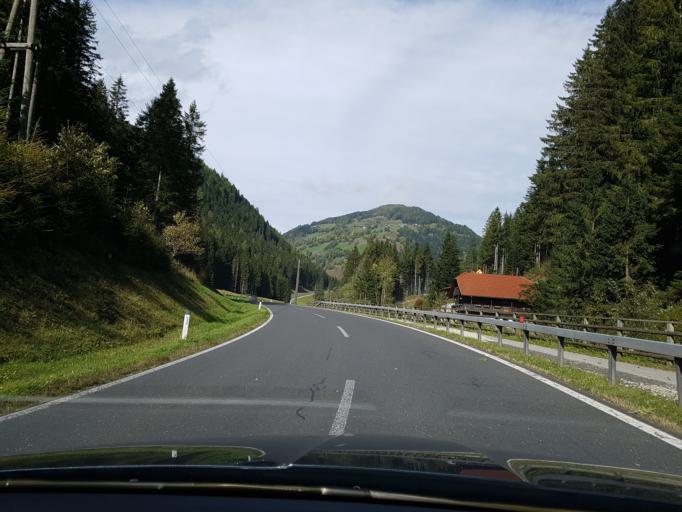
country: AT
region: Carinthia
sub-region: Politischer Bezirk Spittal an der Drau
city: Kleinkirchheim
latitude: 46.8628
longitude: 13.8906
